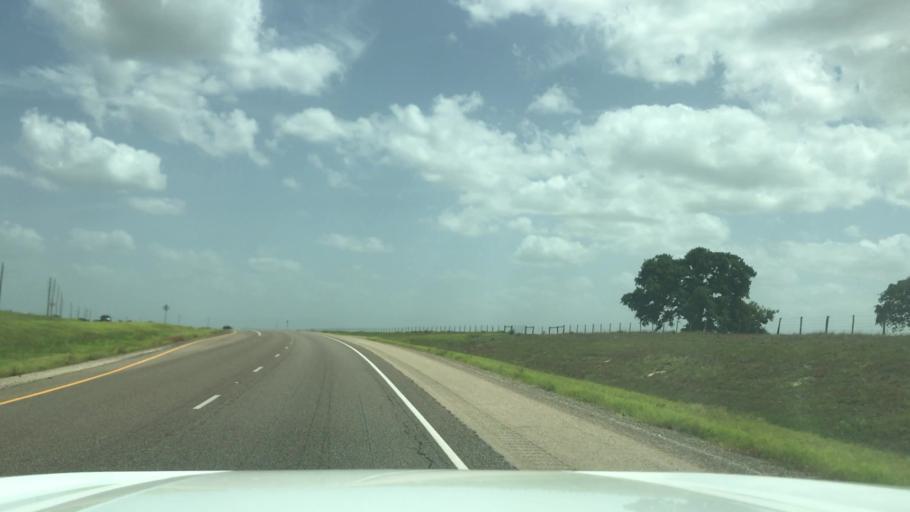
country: US
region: Texas
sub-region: Robertson County
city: Calvert
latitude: 31.0082
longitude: -96.7017
